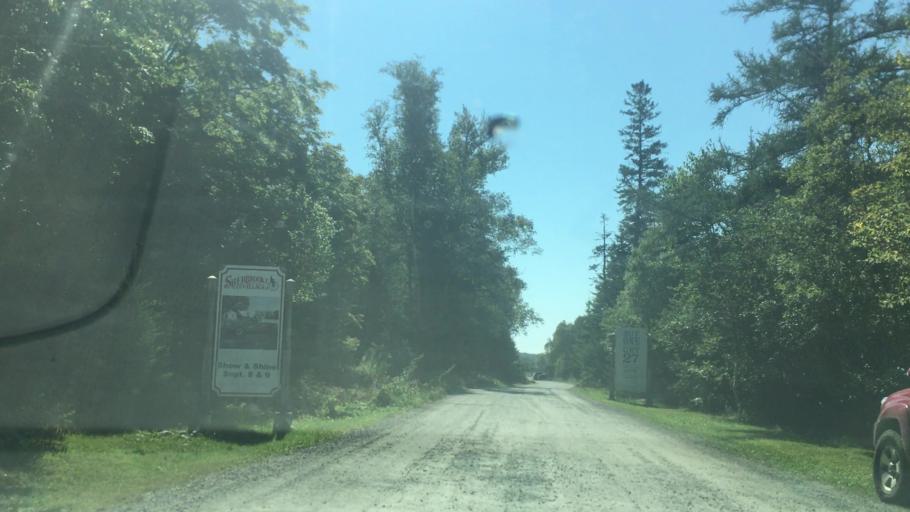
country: CA
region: Nova Scotia
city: Antigonish
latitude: 45.1403
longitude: -61.9828
